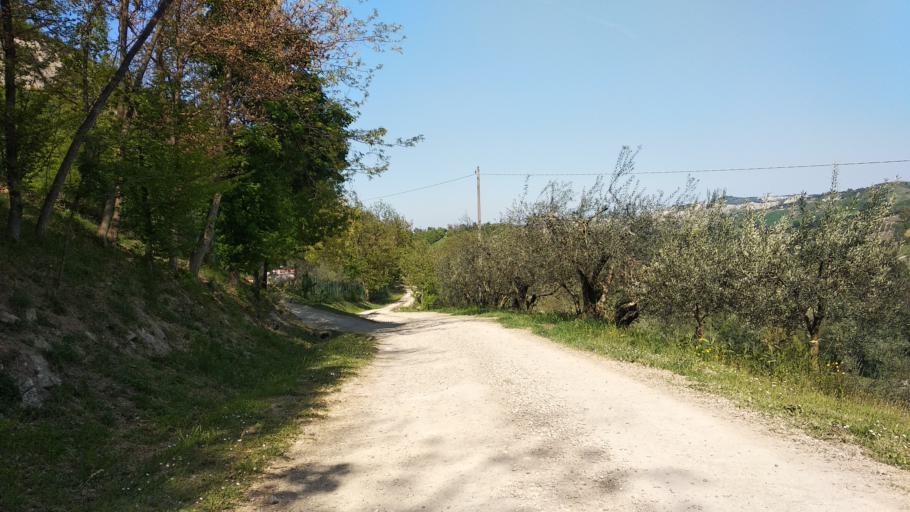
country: IT
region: Emilia-Romagna
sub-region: Provincia di Ravenna
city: Fognano
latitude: 44.2358
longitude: 11.7099
